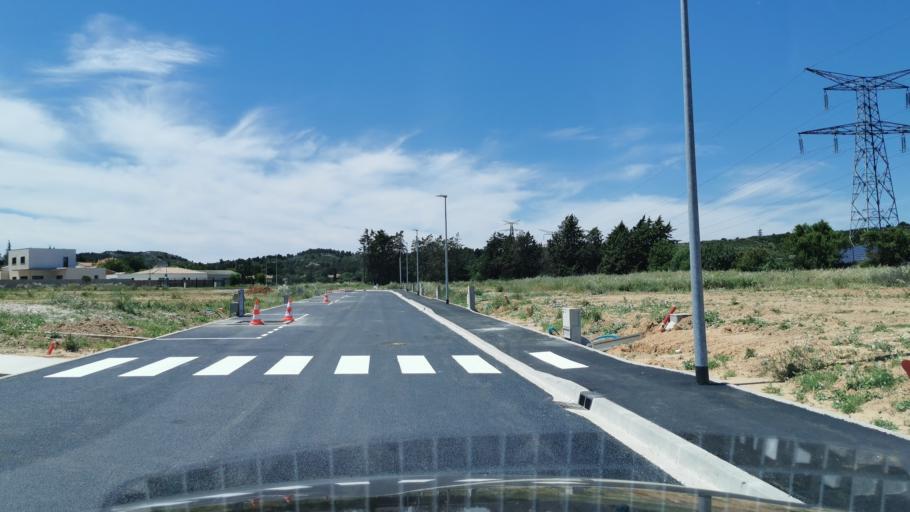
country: FR
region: Languedoc-Roussillon
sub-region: Departement de l'Aude
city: Narbonne
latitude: 43.2024
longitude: 2.9792
